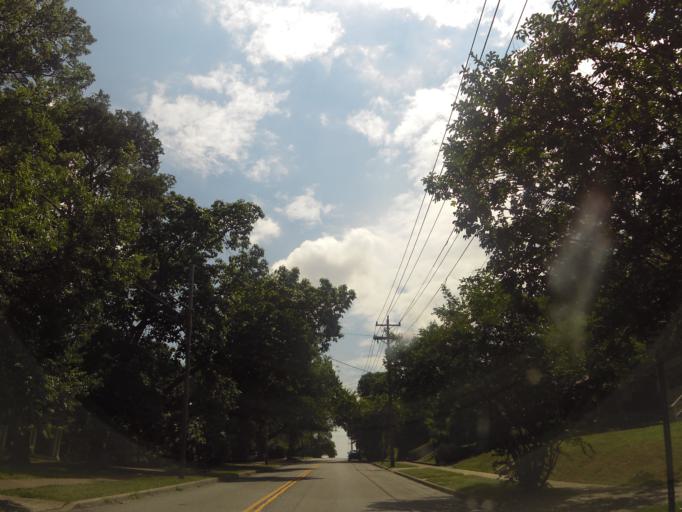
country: US
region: Tennessee
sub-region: Davidson County
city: Nashville
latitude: 36.1301
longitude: -86.8004
